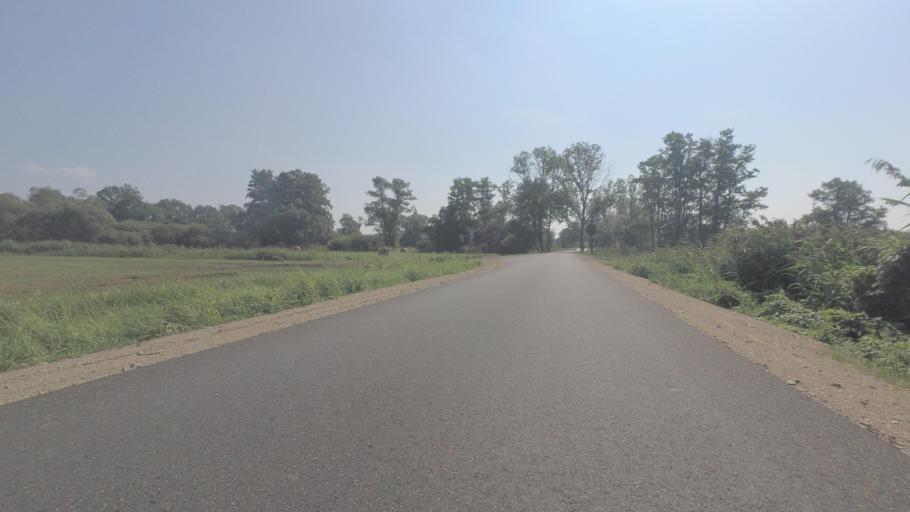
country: DE
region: Mecklenburg-Vorpommern
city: Gielow
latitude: 53.7248
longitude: 12.6784
